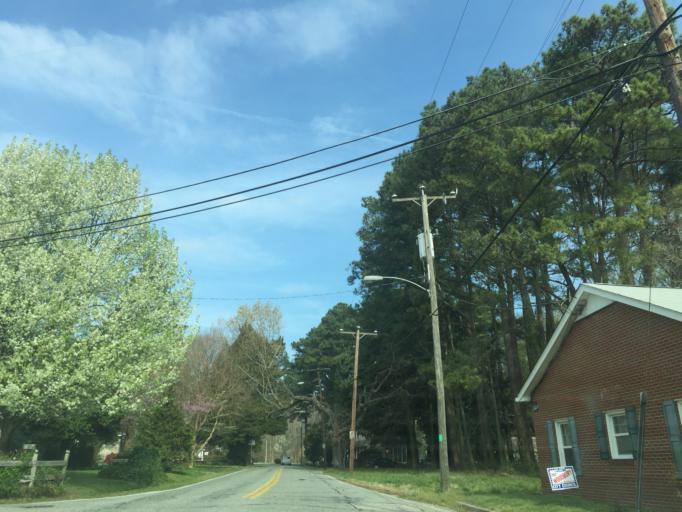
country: US
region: Virginia
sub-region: City of Newport News
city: Newport News
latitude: 37.0546
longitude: -76.4752
